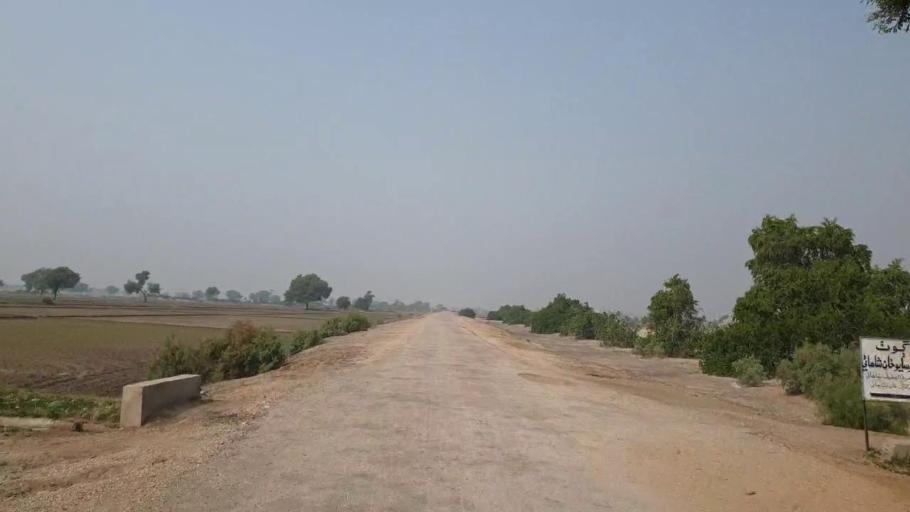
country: PK
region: Sindh
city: Bhan
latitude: 26.4994
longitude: 67.6958
